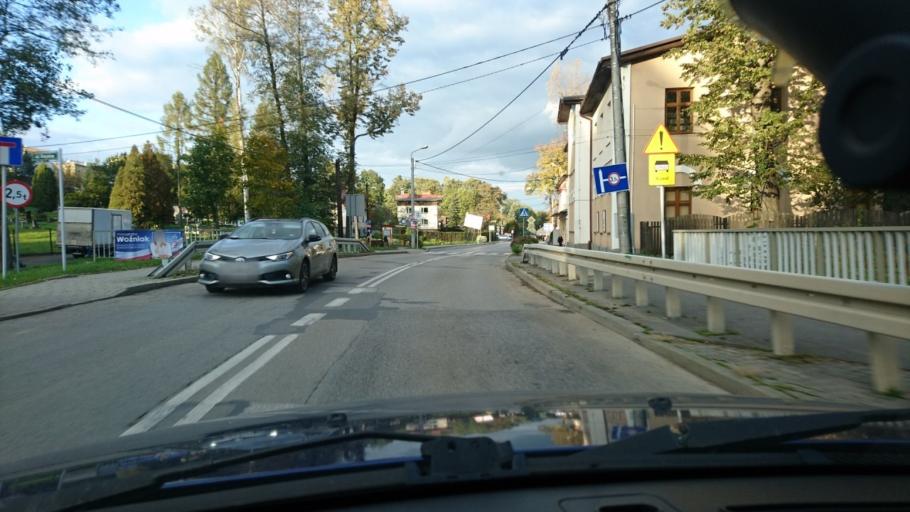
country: PL
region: Silesian Voivodeship
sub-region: Bielsko-Biala
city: Bielsko-Biala
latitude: 49.8015
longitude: 19.0193
